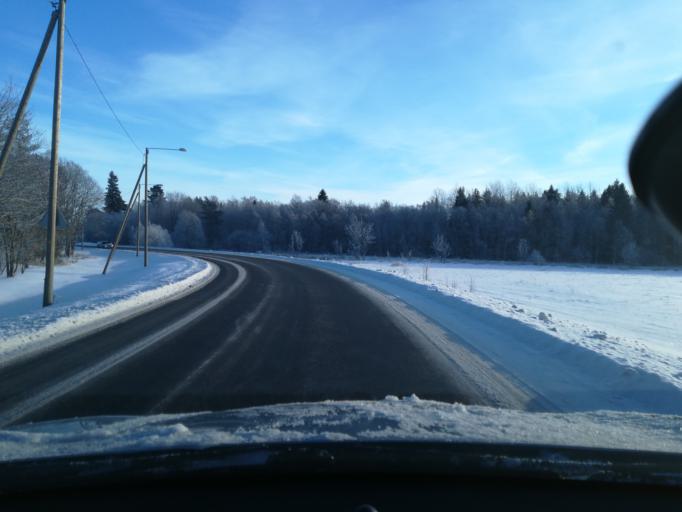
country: EE
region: Harju
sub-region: Keila linn
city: Keila
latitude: 59.3868
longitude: 24.4126
